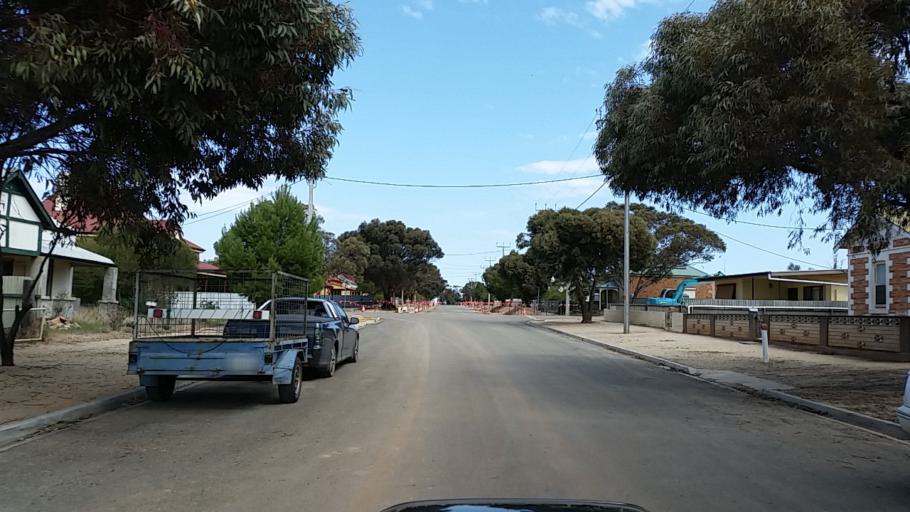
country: AU
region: South Australia
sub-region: Peterborough
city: Peterborough
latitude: -32.9752
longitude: 138.8371
